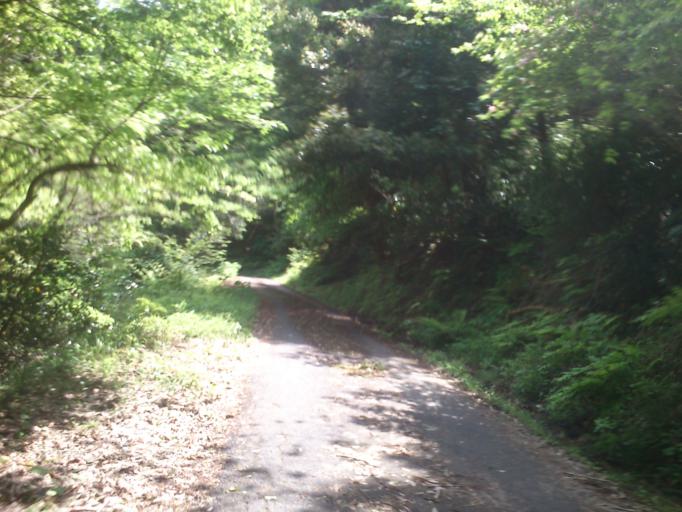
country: JP
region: Kyoto
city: Miyazu
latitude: 35.7018
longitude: 135.1226
